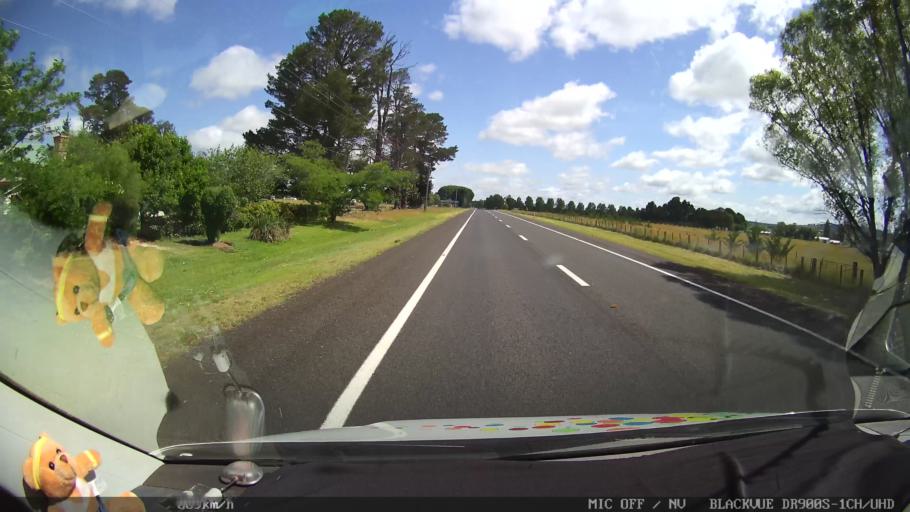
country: AU
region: New South Wales
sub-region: Glen Innes Severn
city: Glen Innes
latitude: -29.8207
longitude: 151.7401
